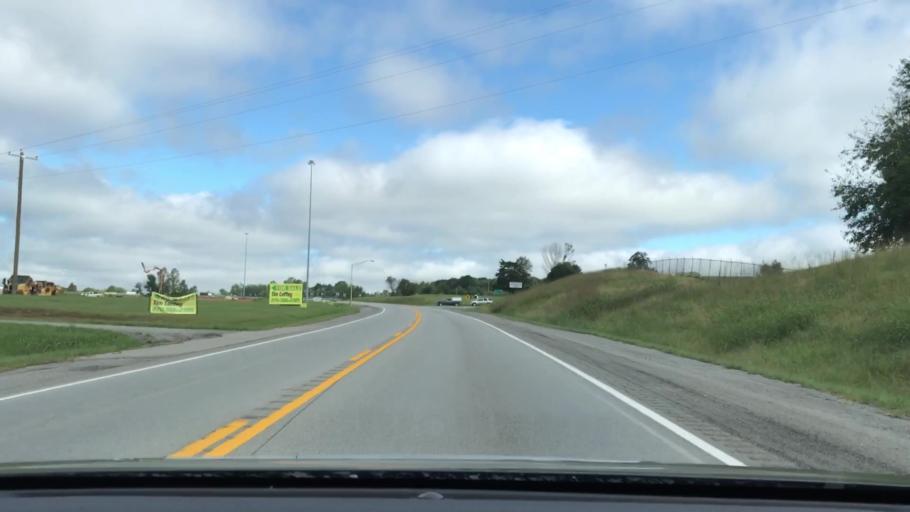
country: US
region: Kentucky
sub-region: Russell County
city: Russell Springs
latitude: 37.0448
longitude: -85.0709
